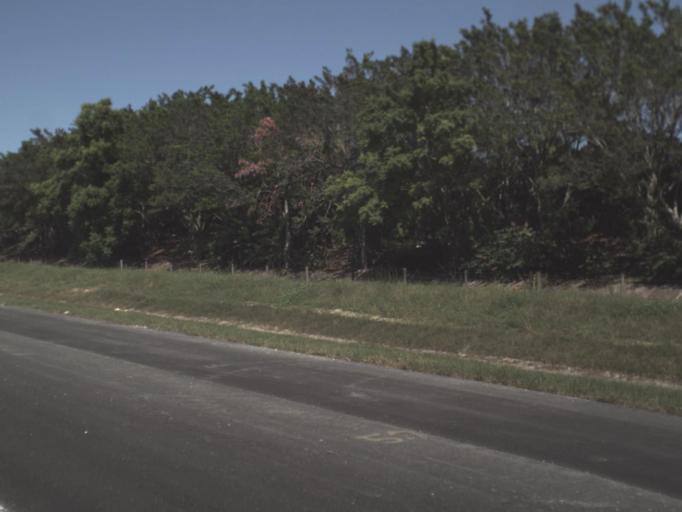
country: US
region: Florida
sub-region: Lee County
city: Three Oaks
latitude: 26.4779
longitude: -81.7922
